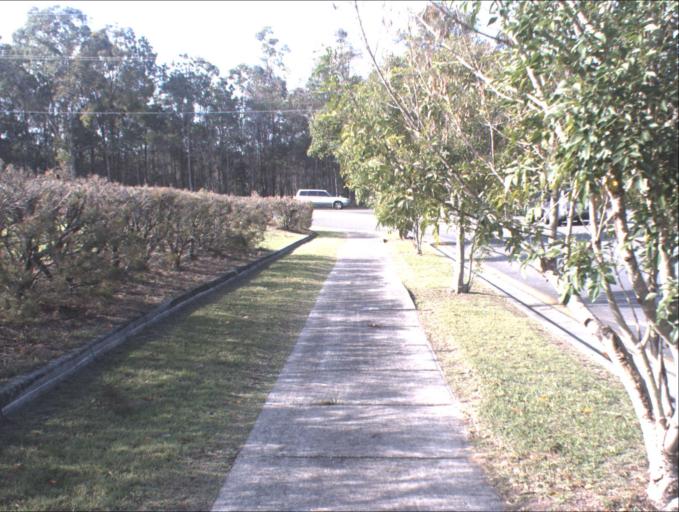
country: AU
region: Queensland
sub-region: Brisbane
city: Forest Lake
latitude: -27.6544
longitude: 152.9962
